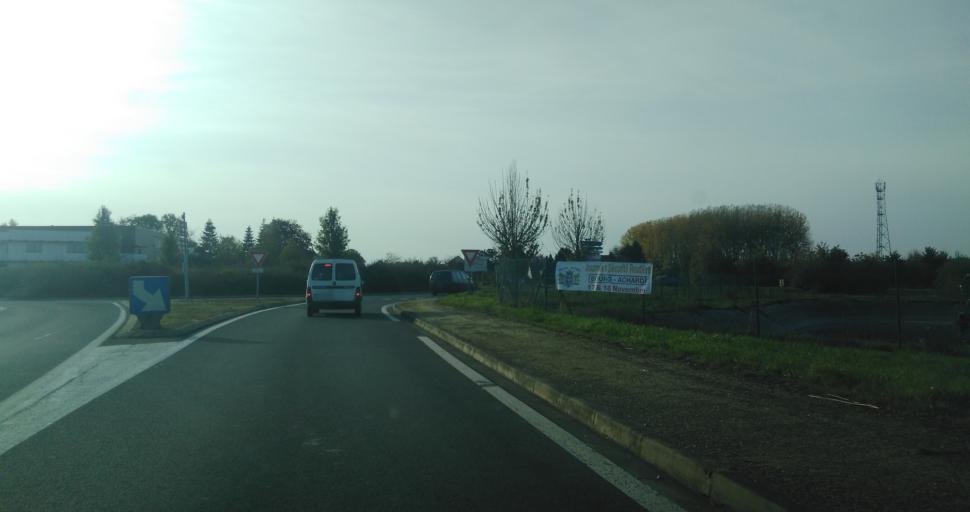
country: FR
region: Haute-Normandie
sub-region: Departement de l'Eure
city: Bourg-Achard
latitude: 49.3575
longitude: 0.8307
